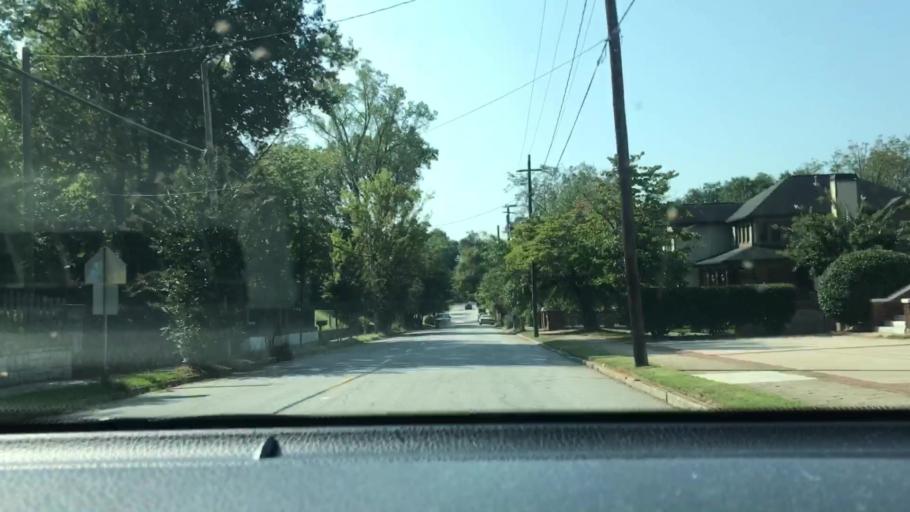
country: US
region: Georgia
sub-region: DeKalb County
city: Druid Hills
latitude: 33.7552
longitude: -84.3232
